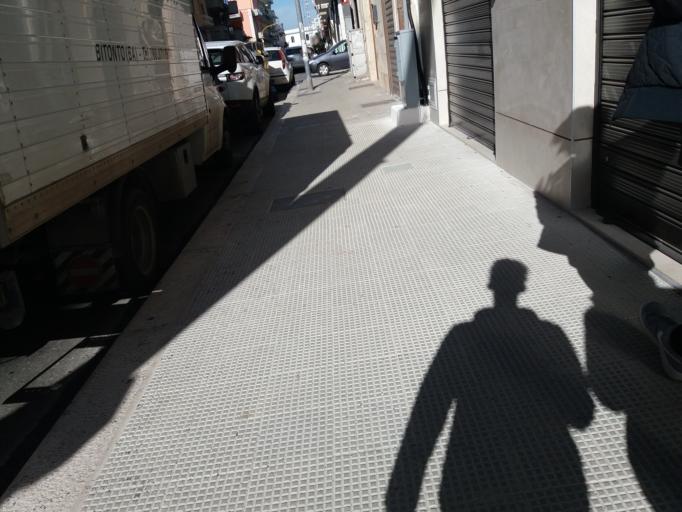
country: IT
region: Apulia
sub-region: Provincia di Bari
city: Bitonto
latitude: 41.1116
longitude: 16.6865
